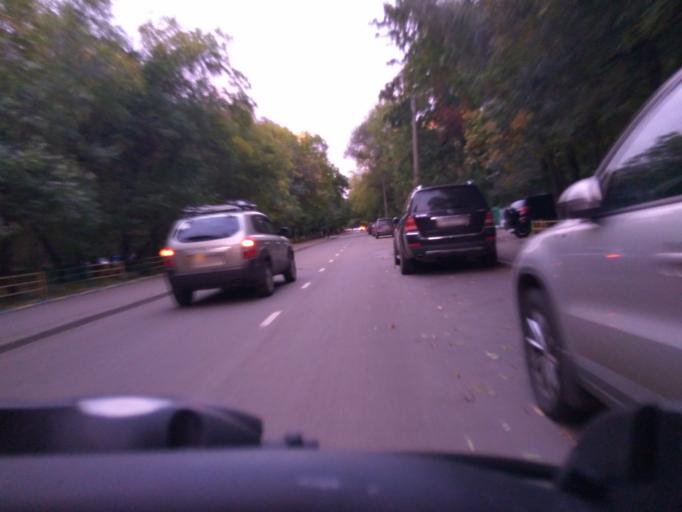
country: RU
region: Moscow
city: Golovinskiy
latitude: 55.8533
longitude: 37.5026
